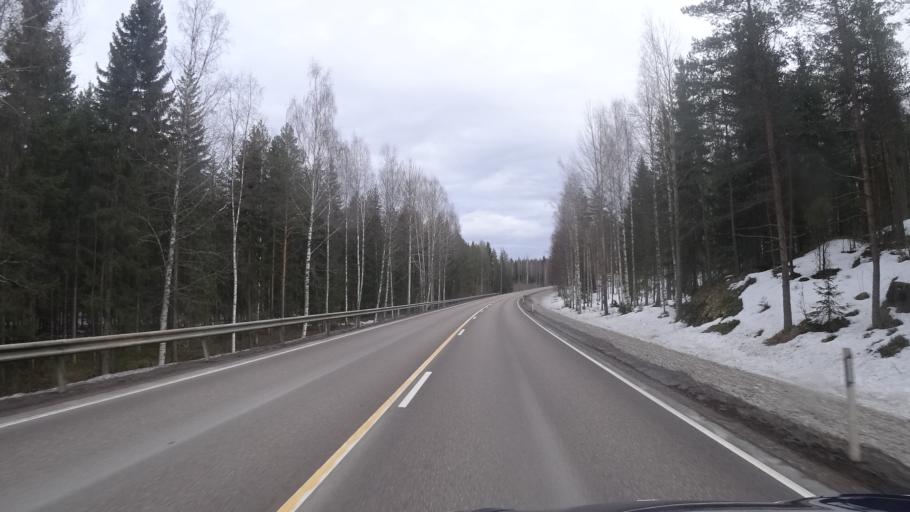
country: FI
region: Kymenlaakso
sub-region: Kouvola
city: Anjala
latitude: 60.6940
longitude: 26.6871
